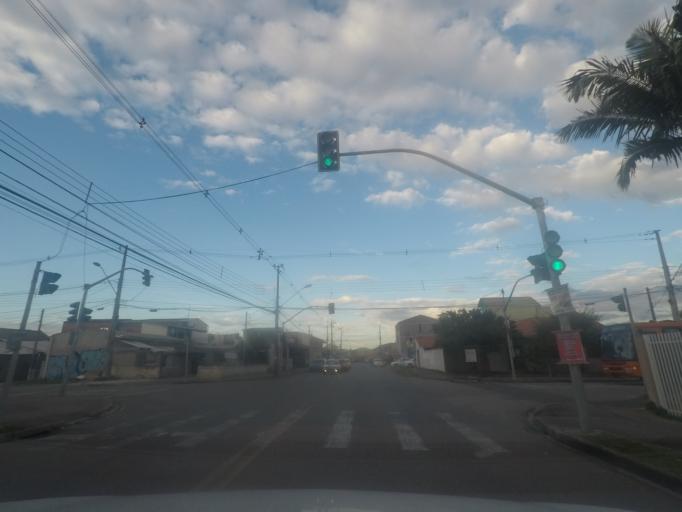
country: BR
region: Parana
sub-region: Pinhais
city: Pinhais
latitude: -25.4707
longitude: -49.2327
